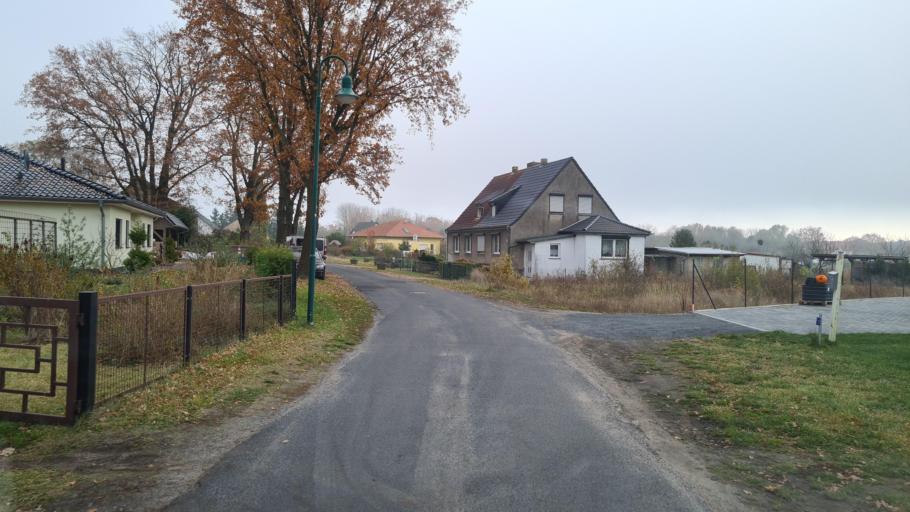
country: DE
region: Brandenburg
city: Gross Kreutz
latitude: 52.3663
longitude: 12.7503
